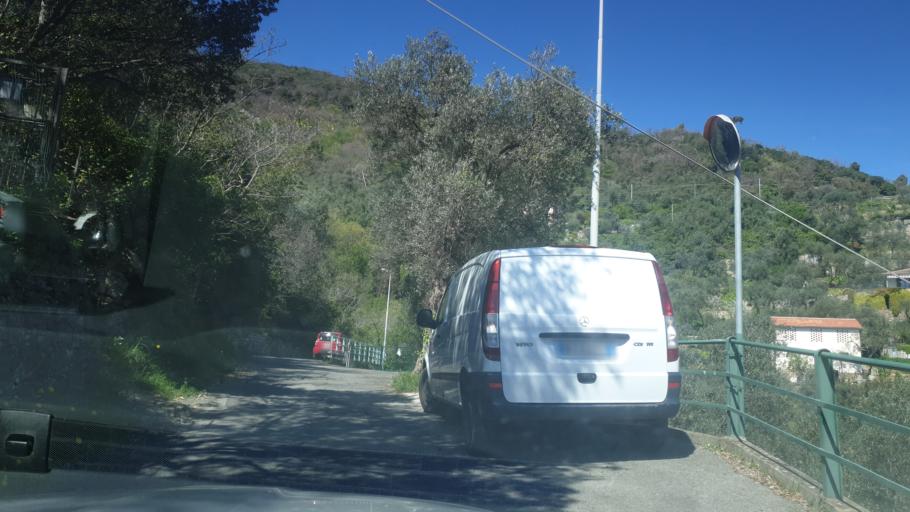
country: IT
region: Liguria
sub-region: Provincia di Genova
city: Recco
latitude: 44.3679
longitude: 9.1429
